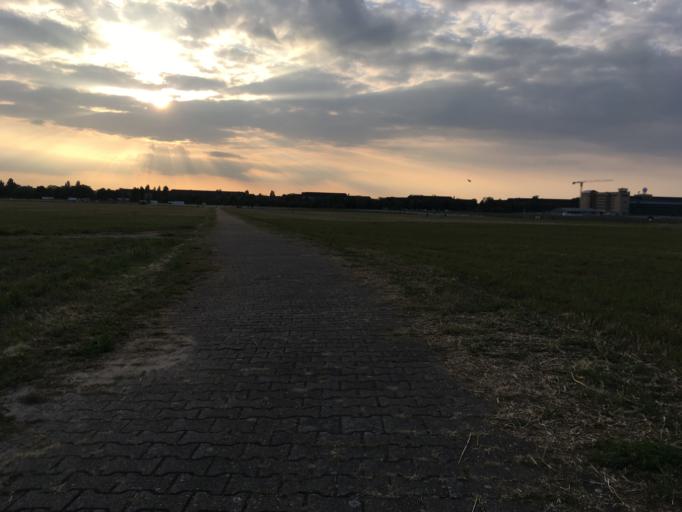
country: DE
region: Berlin
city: Tempelhof Bezirk
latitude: 52.4729
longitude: 13.3971
